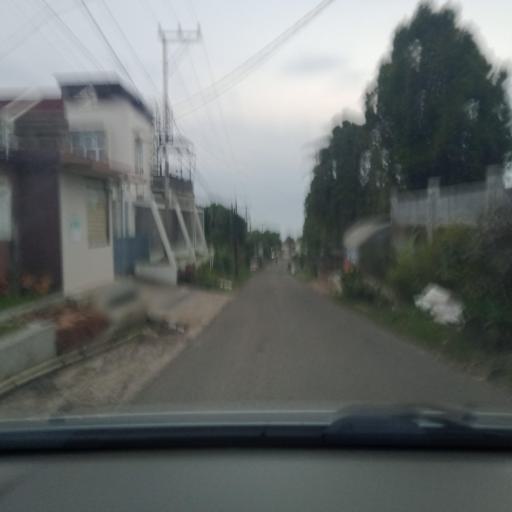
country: ID
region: West Java
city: Lembang
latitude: -6.8269
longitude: 107.5848
